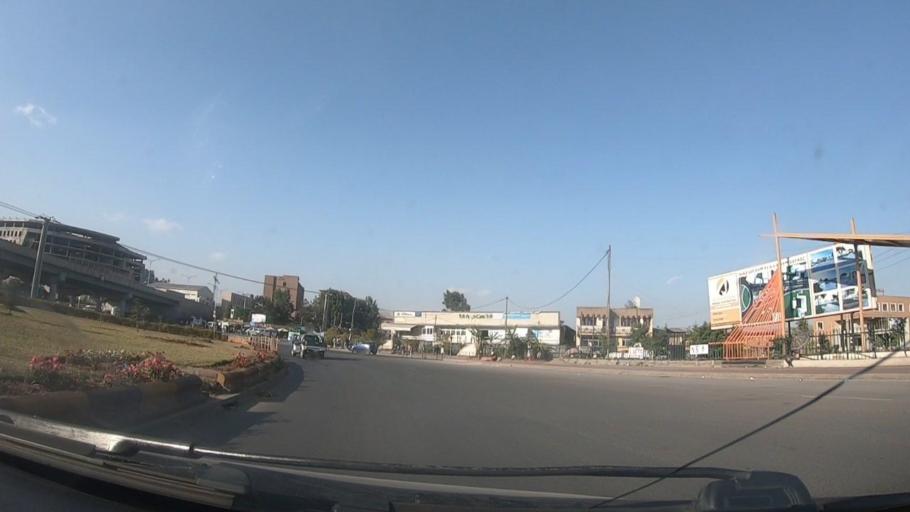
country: ET
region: Adis Abeba
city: Addis Ababa
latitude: 8.9370
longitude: 38.7352
